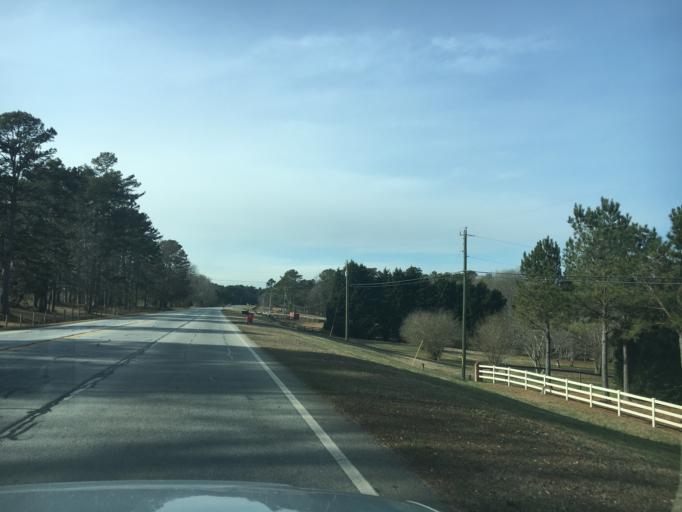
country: US
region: Georgia
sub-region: Jackson County
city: Hoschton
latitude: 34.0698
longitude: -83.7283
